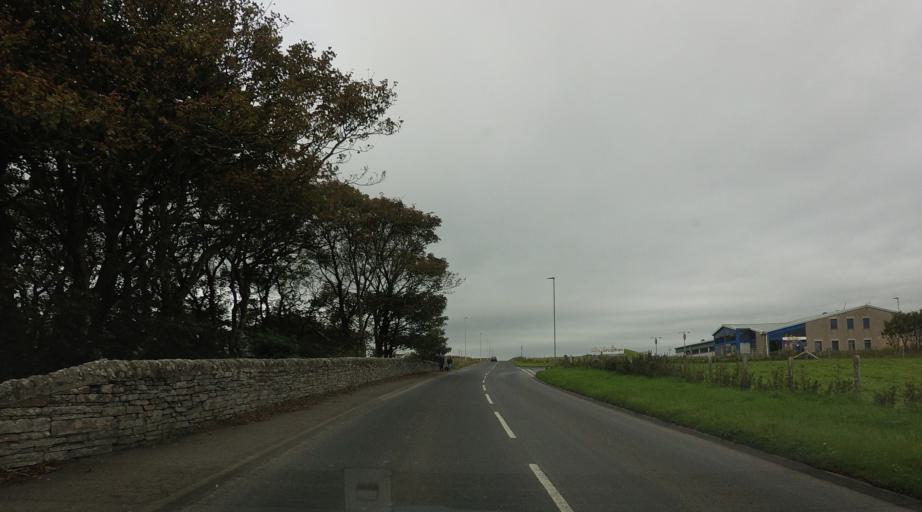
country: GB
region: Scotland
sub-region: Orkney Islands
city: Orkney
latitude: 58.9868
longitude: -2.9769
